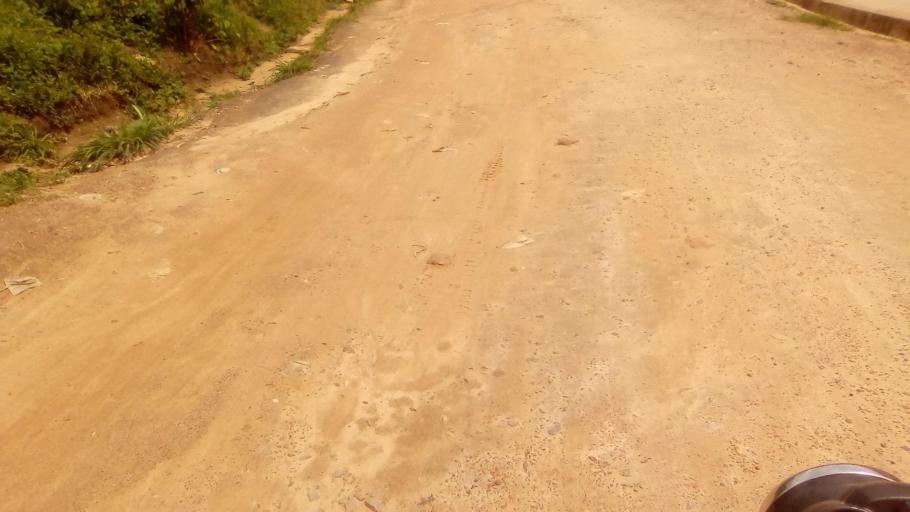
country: SL
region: Southern Province
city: Bo
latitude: 7.9779
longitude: -11.7684
